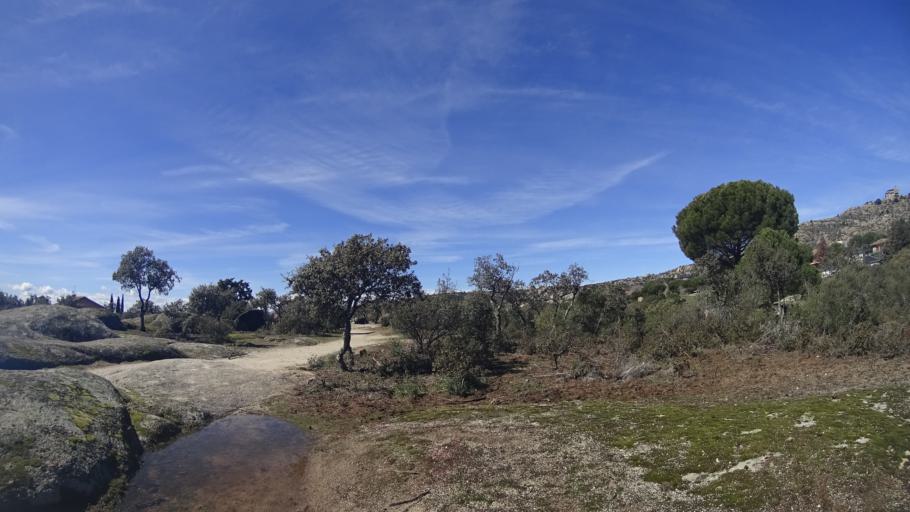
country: ES
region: Madrid
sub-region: Provincia de Madrid
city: Torrelodones
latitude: 40.5816
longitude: -3.9234
